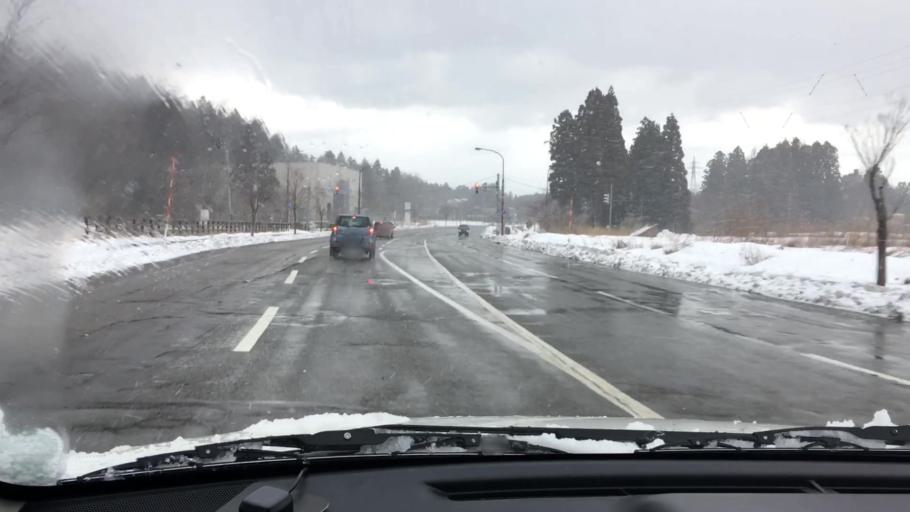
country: JP
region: Niigata
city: Joetsu
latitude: 37.0972
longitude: 138.2310
